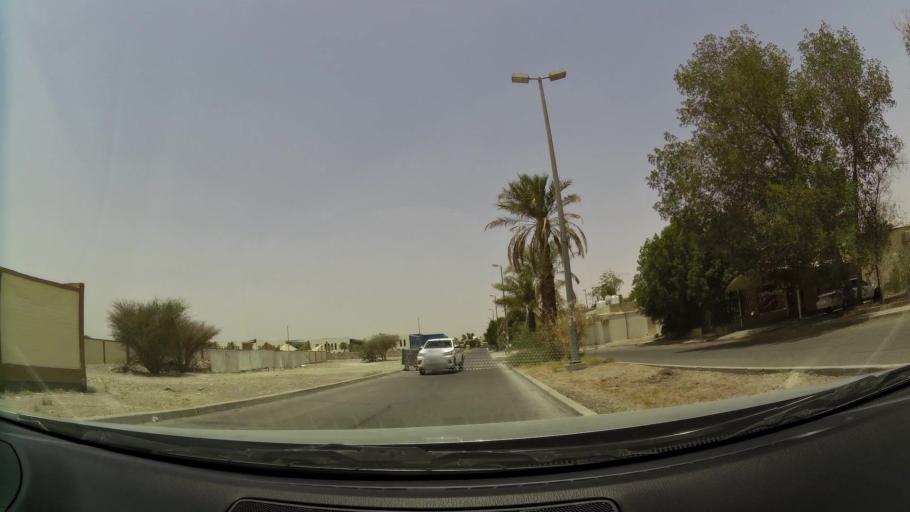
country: AE
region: Abu Dhabi
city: Al Ain
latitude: 24.2102
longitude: 55.7504
